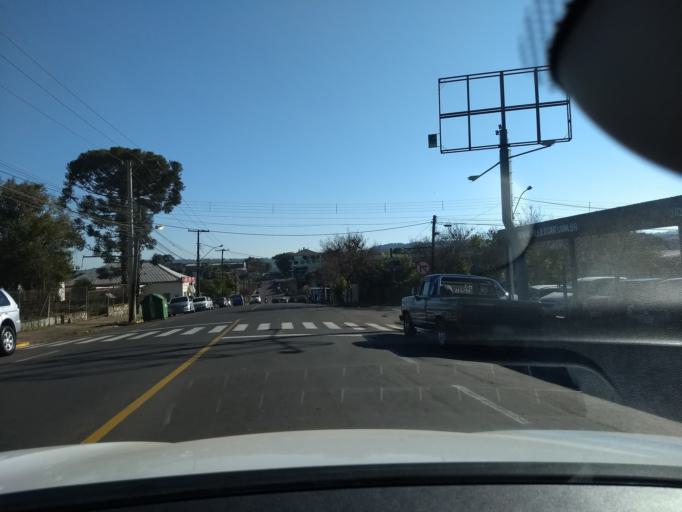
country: BR
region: Rio Grande do Sul
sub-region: Santa Cruz Do Sul
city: Santa Cruz do Sul
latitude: -29.7185
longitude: -52.4415
